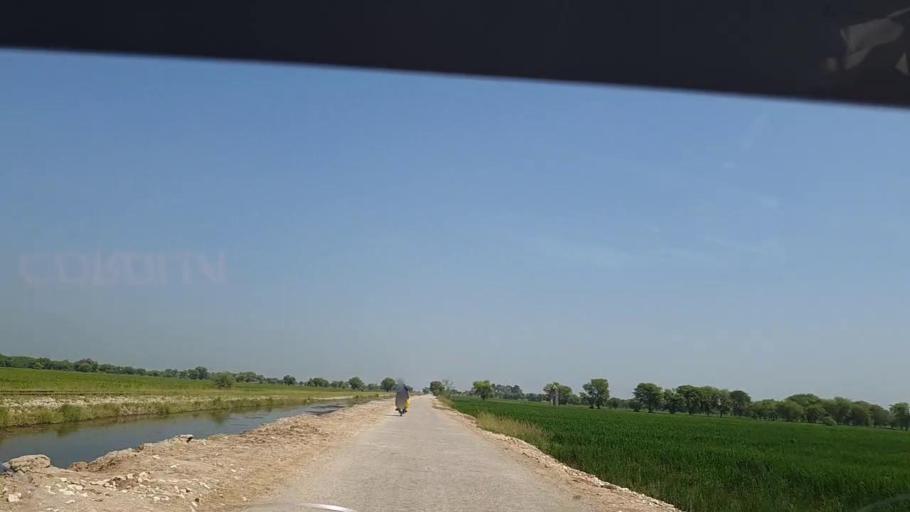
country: PK
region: Sindh
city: Tangwani
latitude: 28.2840
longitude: 69.0243
